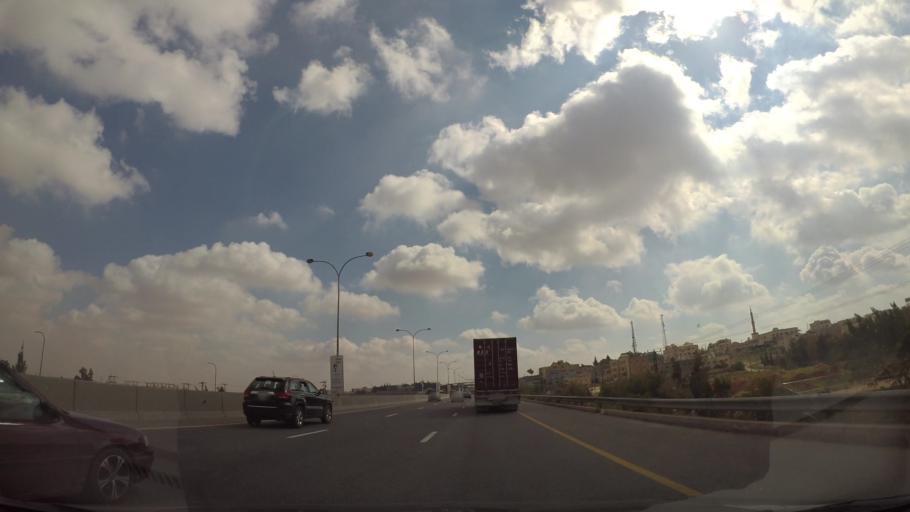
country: JO
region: Amman
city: Al Jizah
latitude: 31.7505
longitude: 35.9412
